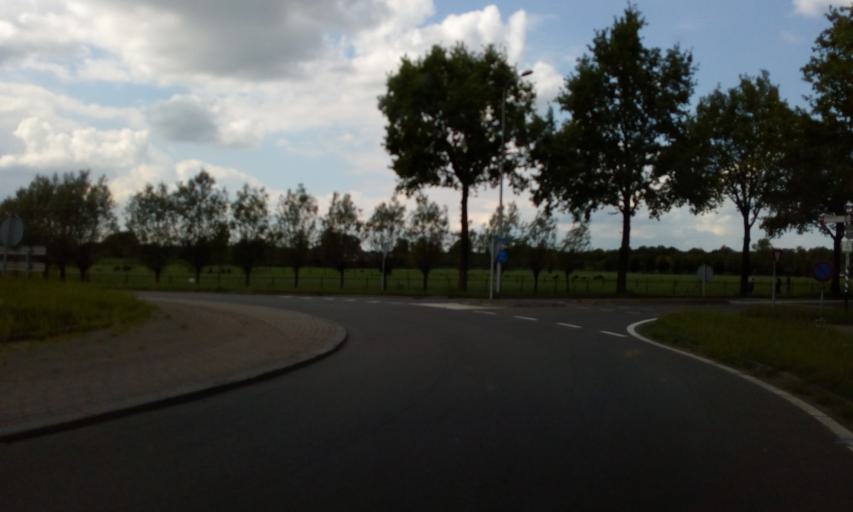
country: NL
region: Gelderland
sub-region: Gemeente Voorst
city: Twello
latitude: 52.1889
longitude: 6.0916
